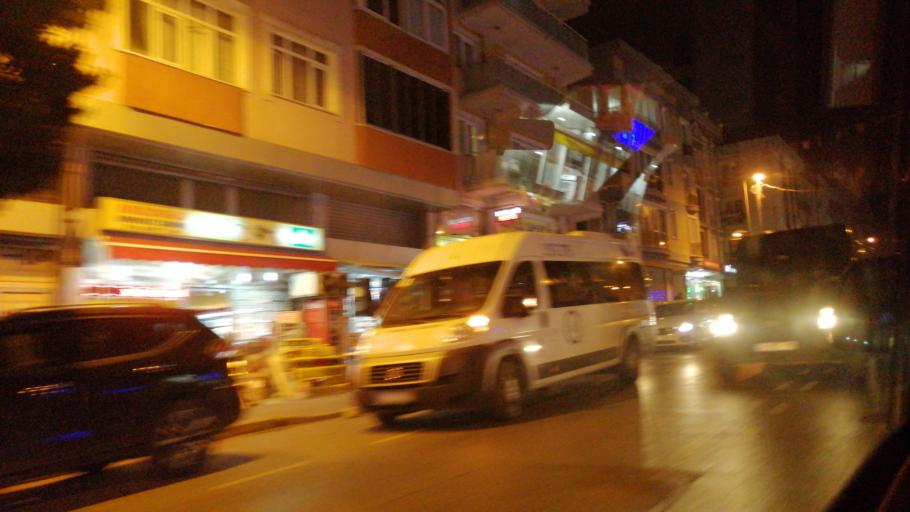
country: TR
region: Istanbul
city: Umraniye
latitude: 41.0108
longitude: 29.1279
